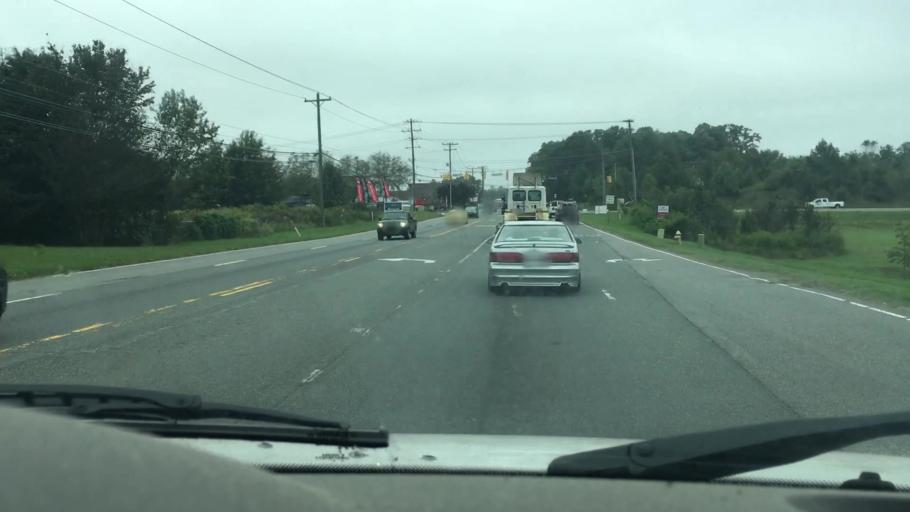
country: US
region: North Carolina
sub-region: Catawba County
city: Lake Norman of Catawba
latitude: 35.6012
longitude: -80.8956
